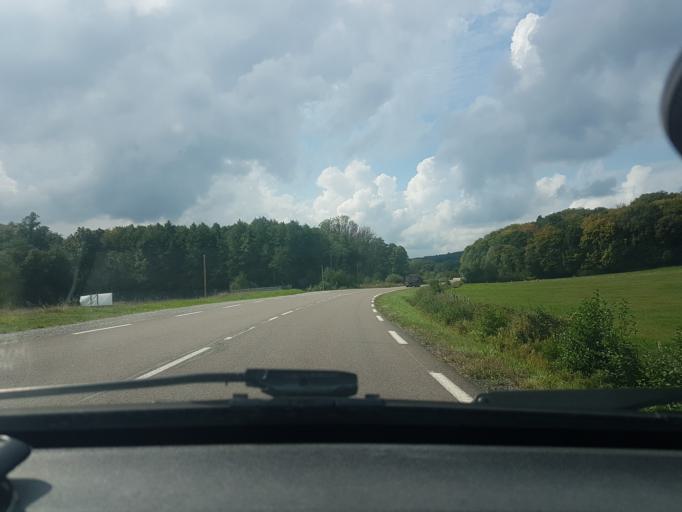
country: FR
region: Franche-Comte
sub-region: Departement de la Haute-Saone
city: Hericourt
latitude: 47.5928
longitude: 6.7152
